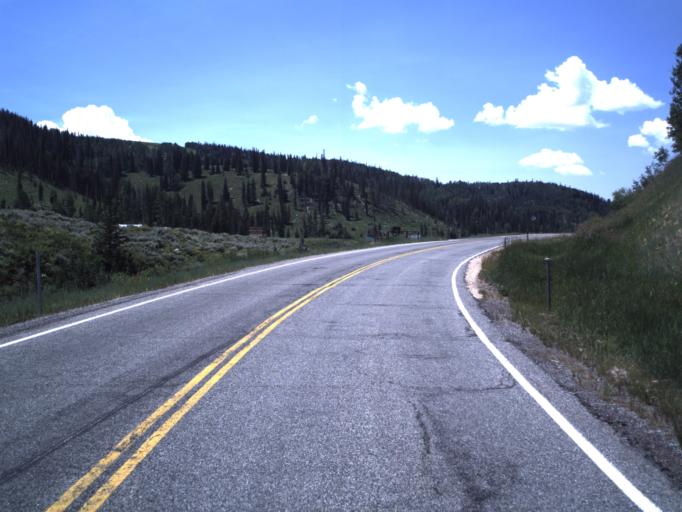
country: US
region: Utah
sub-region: Sanpete County
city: Fairview
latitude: 39.6477
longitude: -111.2584
